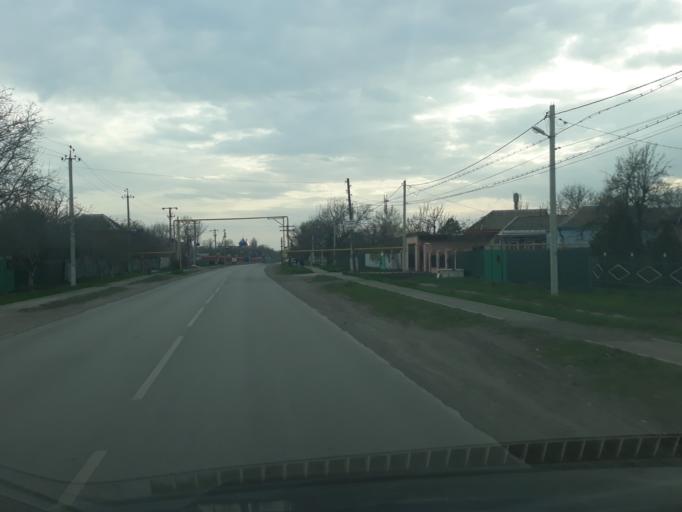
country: RU
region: Rostov
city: Novobessergenovka
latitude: 47.1703
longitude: 38.7444
